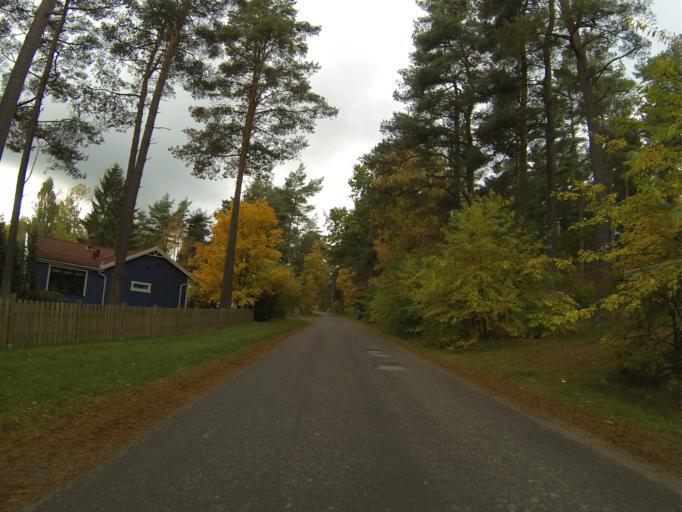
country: SE
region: Skane
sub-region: Sjobo Kommun
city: Sjoebo
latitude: 55.6309
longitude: 13.6628
